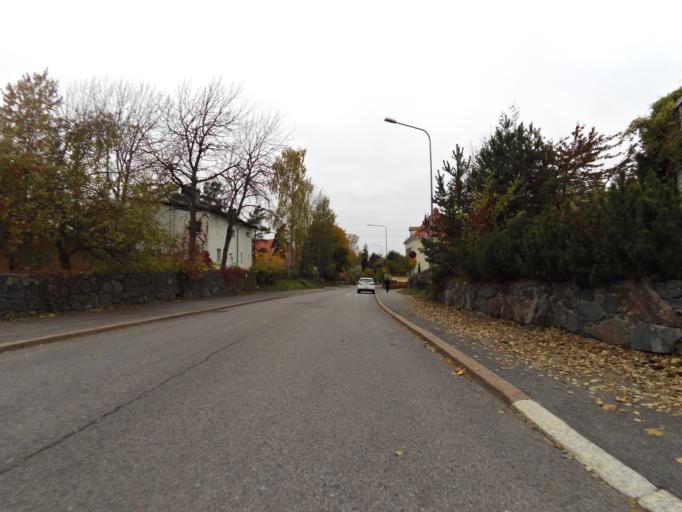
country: FI
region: Uusimaa
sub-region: Helsinki
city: Helsinki
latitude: 60.1843
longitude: 25.0047
